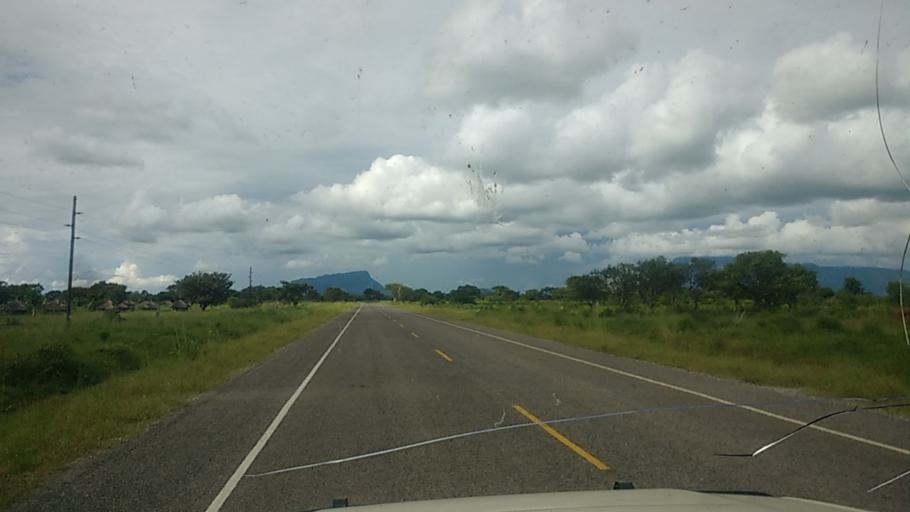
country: UG
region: Eastern Region
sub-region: Katakwi District
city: Katakwi
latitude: 2.0121
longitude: 34.1051
